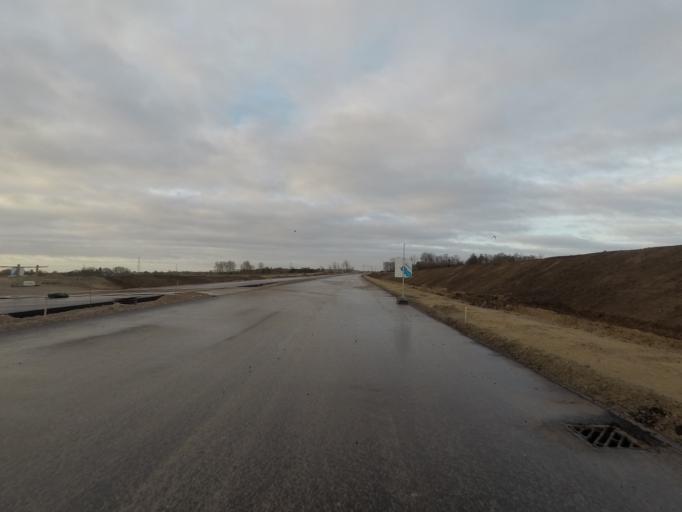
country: DK
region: Capital Region
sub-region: Frederikssund Kommune
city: Frederikssund
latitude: 55.8066
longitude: 12.0168
